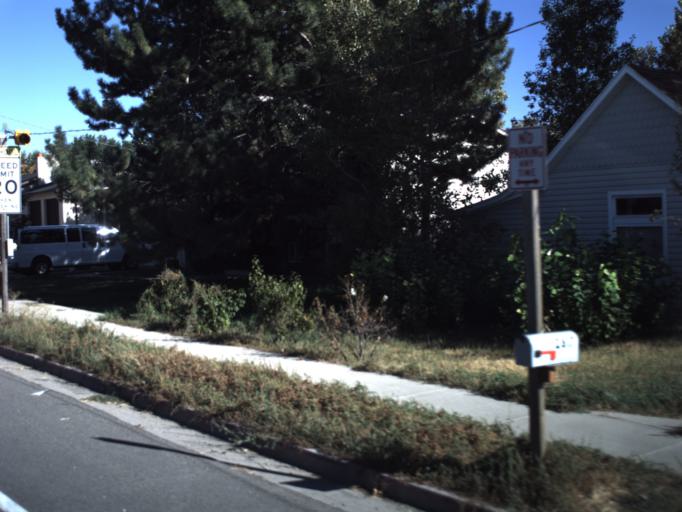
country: US
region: Utah
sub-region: Davis County
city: West Point
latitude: 41.1399
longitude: -112.0804
